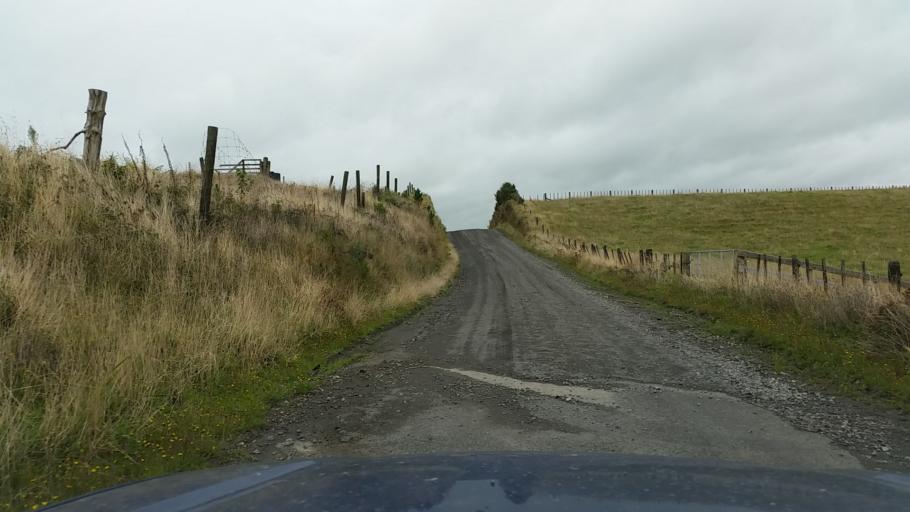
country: NZ
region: Taranaki
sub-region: South Taranaki District
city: Eltham
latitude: -39.2776
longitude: 174.3078
